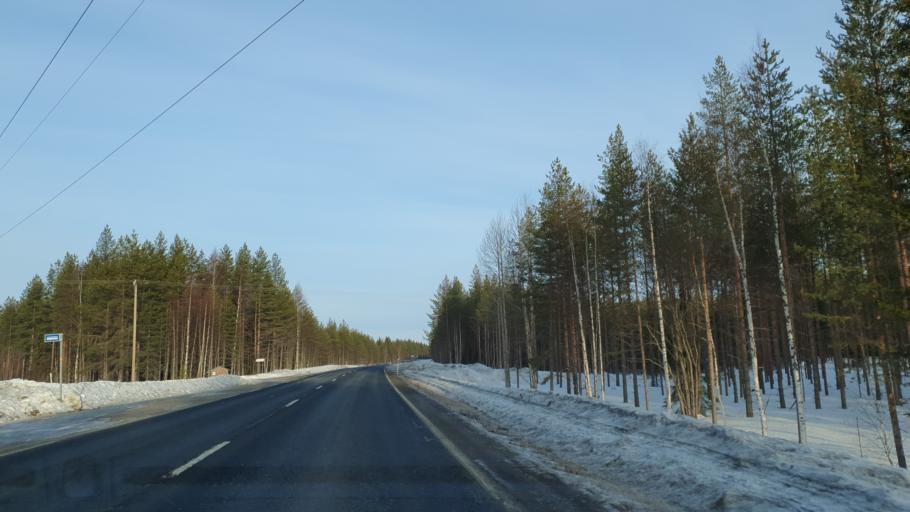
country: FI
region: Kainuu
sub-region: Kehys-Kainuu
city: Kuhmo
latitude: 64.0980
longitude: 29.3788
